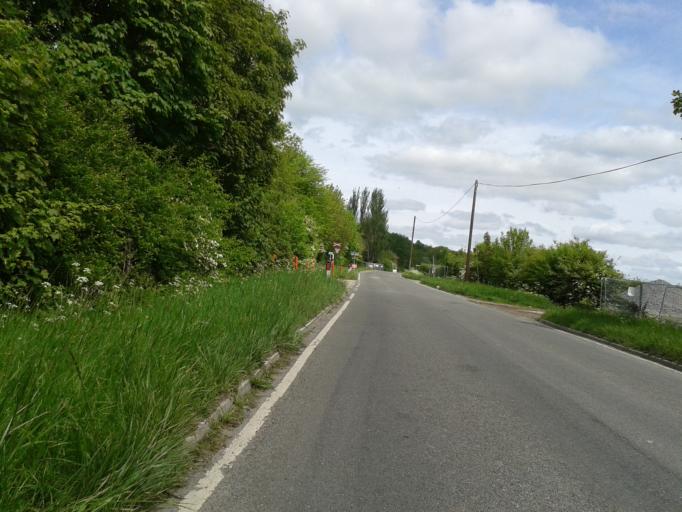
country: GB
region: England
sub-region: Cambridgeshire
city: Haslingfield
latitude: 52.1348
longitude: 0.0404
